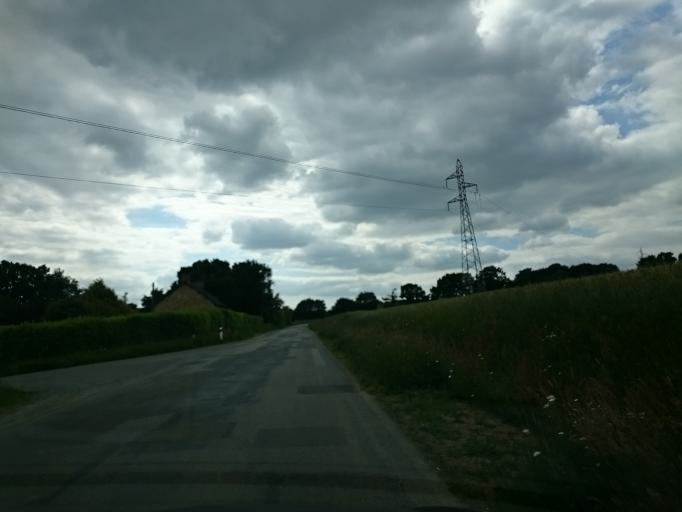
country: FR
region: Brittany
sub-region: Departement d'Ille-et-Vilaine
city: Chanteloup
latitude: 47.9276
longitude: -1.6232
